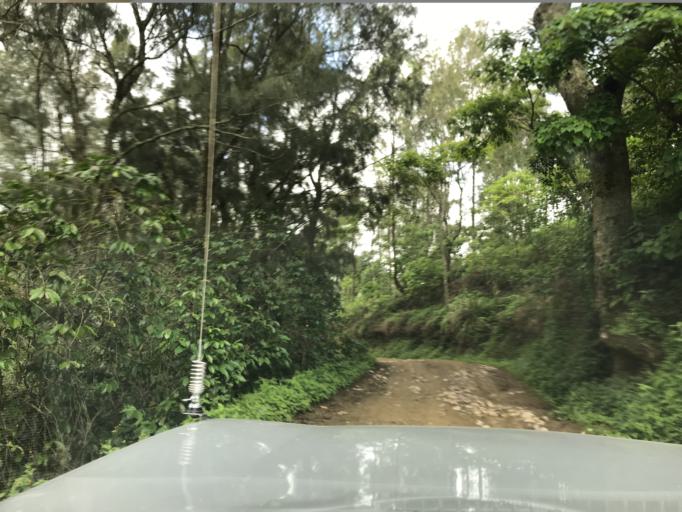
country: TL
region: Aileu
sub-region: Aileu Villa
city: Aileu
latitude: -8.8587
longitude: 125.5755
